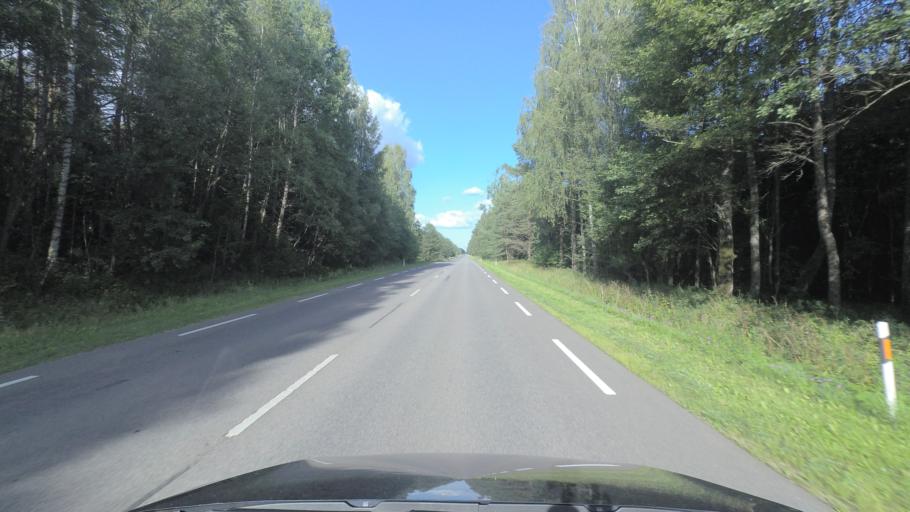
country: LT
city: Pabrade
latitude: 54.9656
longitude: 25.7116
